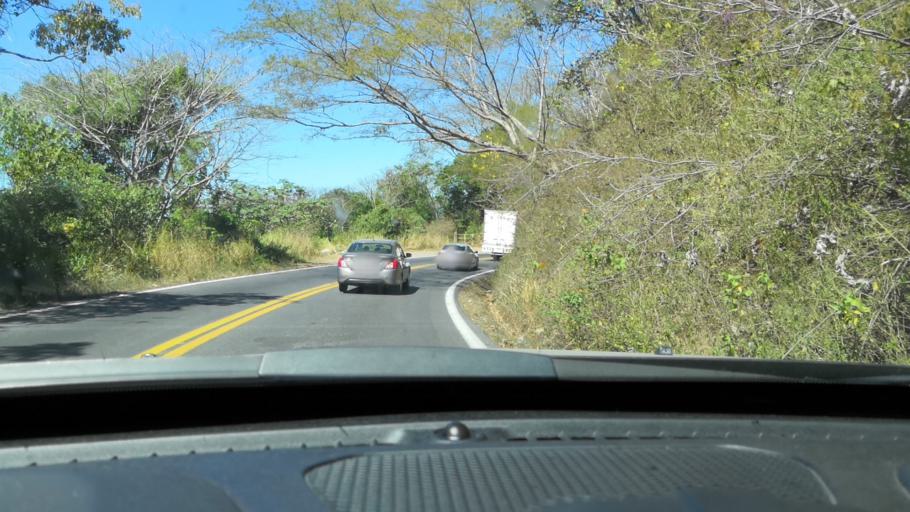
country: MX
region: Nayarit
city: Compostela
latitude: 21.2149
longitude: -104.9936
